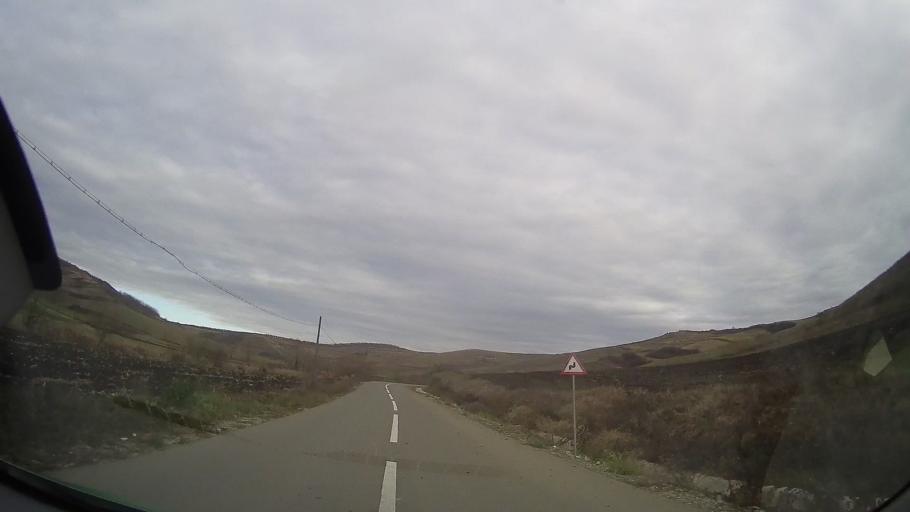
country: RO
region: Bistrita-Nasaud
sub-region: Comuna Silvasu de Campie
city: Silvasu de Campie
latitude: 46.8209
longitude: 24.2991
